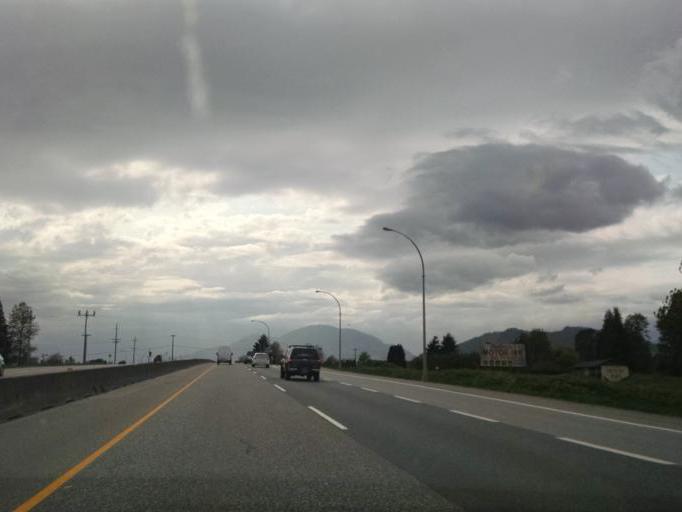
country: CA
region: British Columbia
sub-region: Fraser Valley Regional District
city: Chilliwack
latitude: 49.1493
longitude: -121.9439
